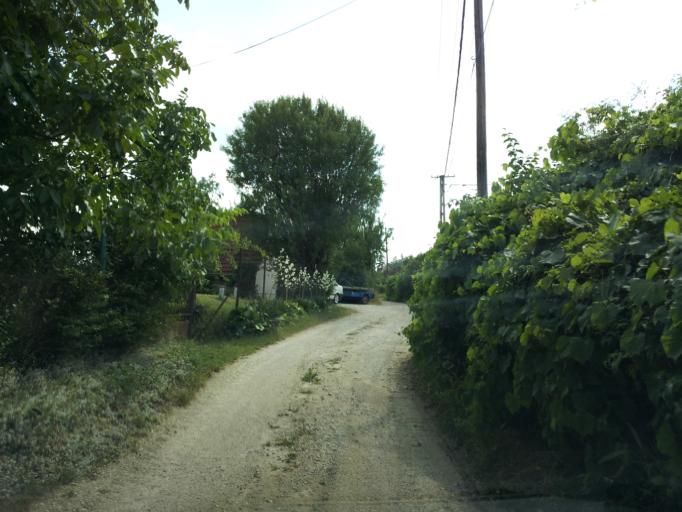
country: HU
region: Veszprem
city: Balatonalmadi
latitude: 47.0583
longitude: 18.0189
